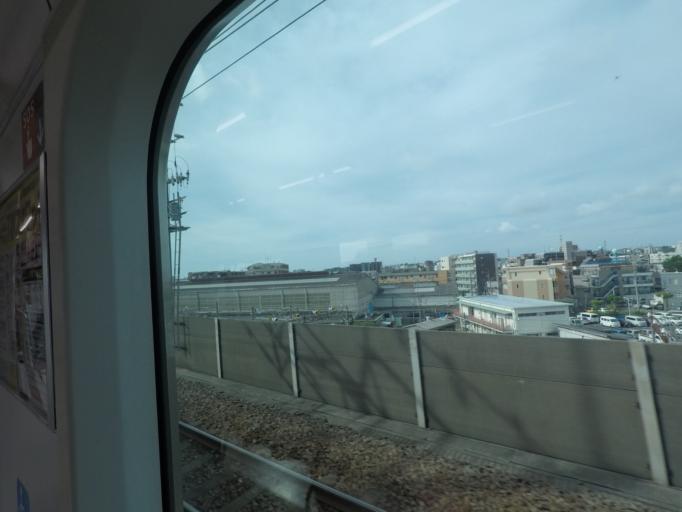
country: JP
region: Kanagawa
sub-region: Kawasaki-shi
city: Kawasaki
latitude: 35.5851
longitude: 139.6339
